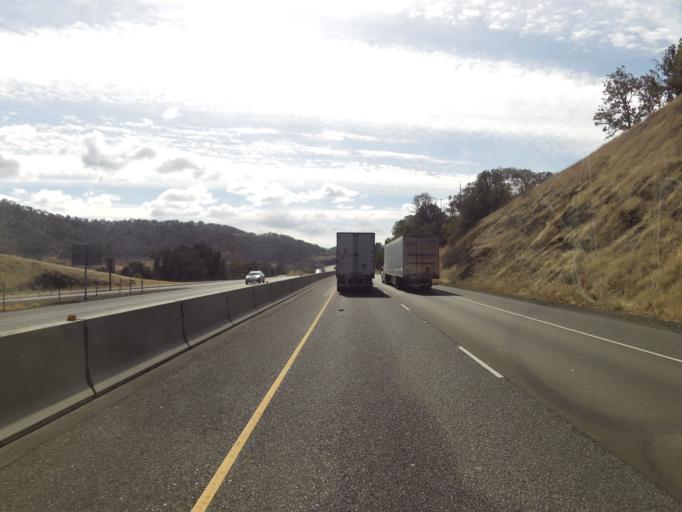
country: US
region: Oregon
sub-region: Douglas County
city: Green
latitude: 43.1766
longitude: -123.3715
